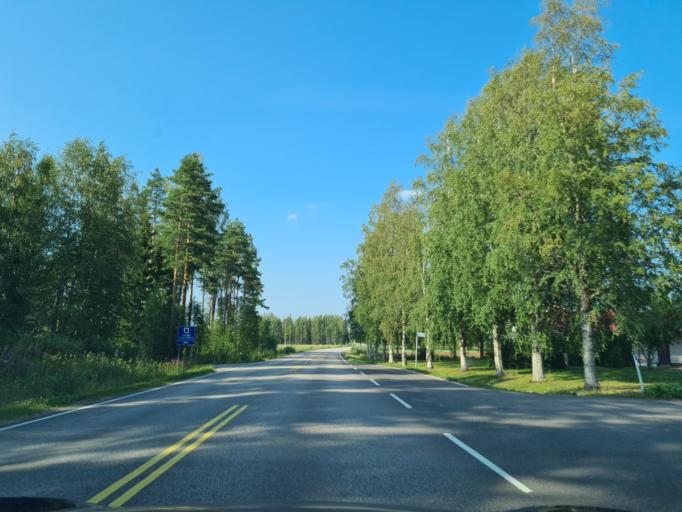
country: FI
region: Satakunta
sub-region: Pohjois-Satakunta
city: Karvia
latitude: 62.1859
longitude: 22.5948
